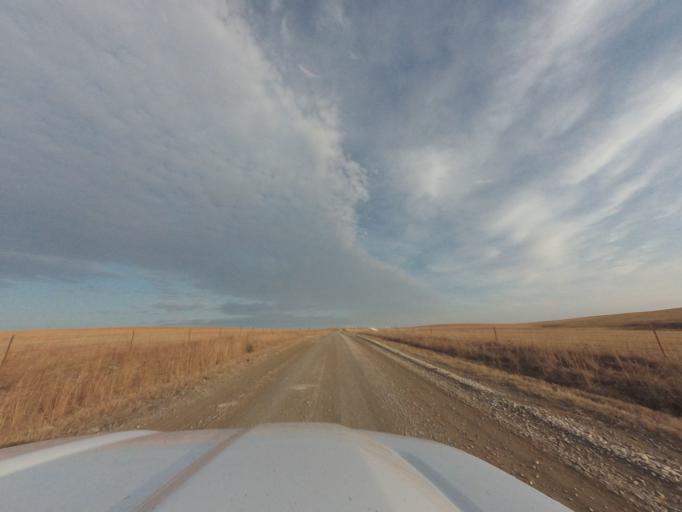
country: US
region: Kansas
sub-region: Morris County
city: Council Grove
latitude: 38.5058
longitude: -96.4102
